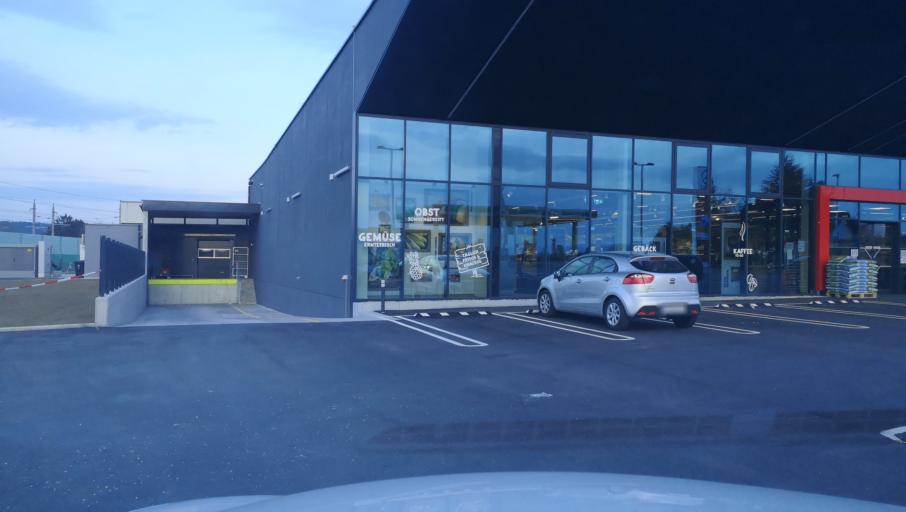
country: AT
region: Lower Austria
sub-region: Politischer Bezirk Melk
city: Blindenmarkt
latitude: 48.1244
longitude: 14.9736
